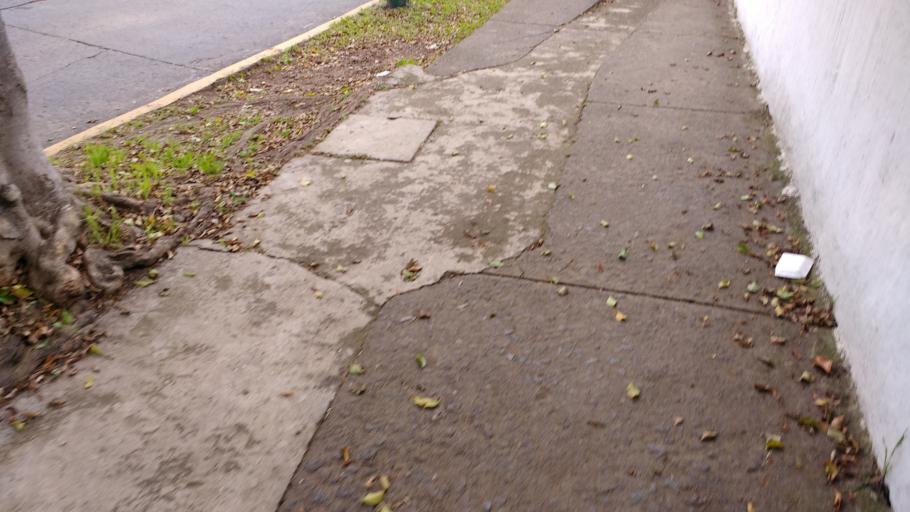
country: MX
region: Veracruz
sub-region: Xalapa
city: Xalapa de Enriquez
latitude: 19.5353
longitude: -96.9172
